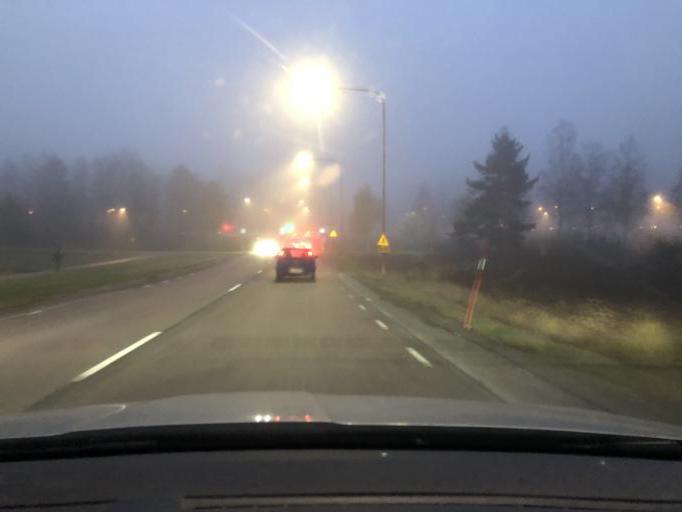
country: SE
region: Stockholm
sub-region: Huddinge Kommun
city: Huddinge
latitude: 59.2288
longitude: 17.9372
